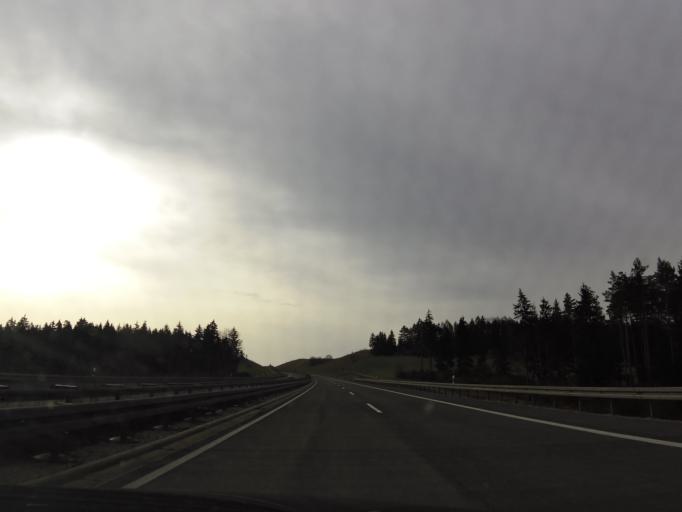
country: DE
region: Thuringia
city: Veilsdorf
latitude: 50.4729
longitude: 10.8259
